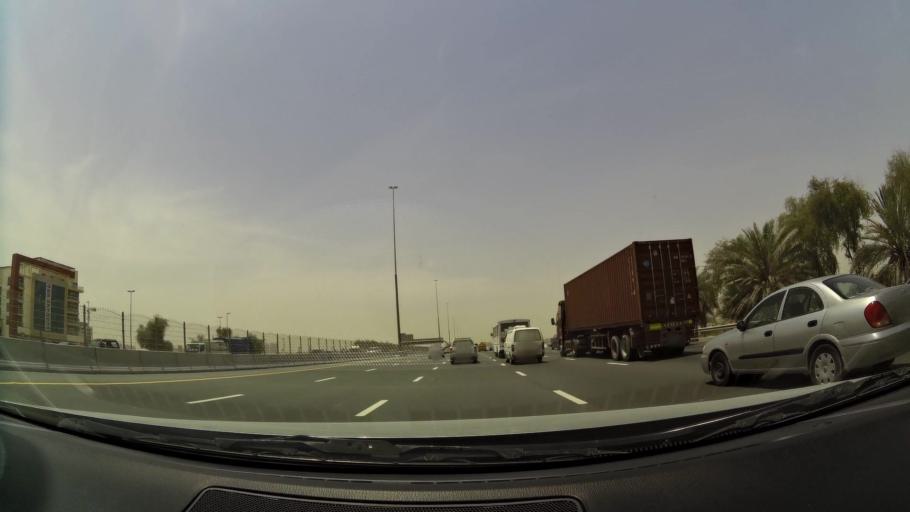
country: AE
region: Ash Shariqah
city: Sharjah
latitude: 25.1503
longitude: 55.3869
